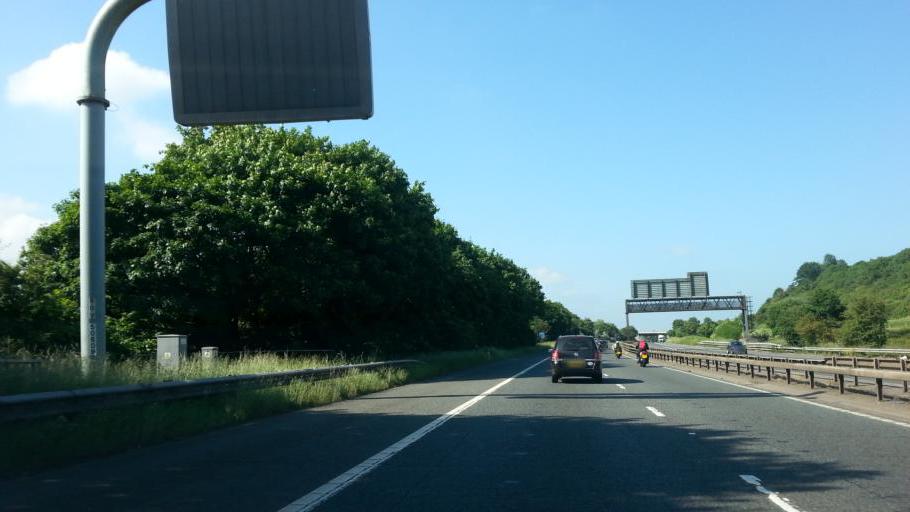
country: GB
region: England
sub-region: South Gloucestershire
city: Stoke Gifford
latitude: 51.4972
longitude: -2.5336
